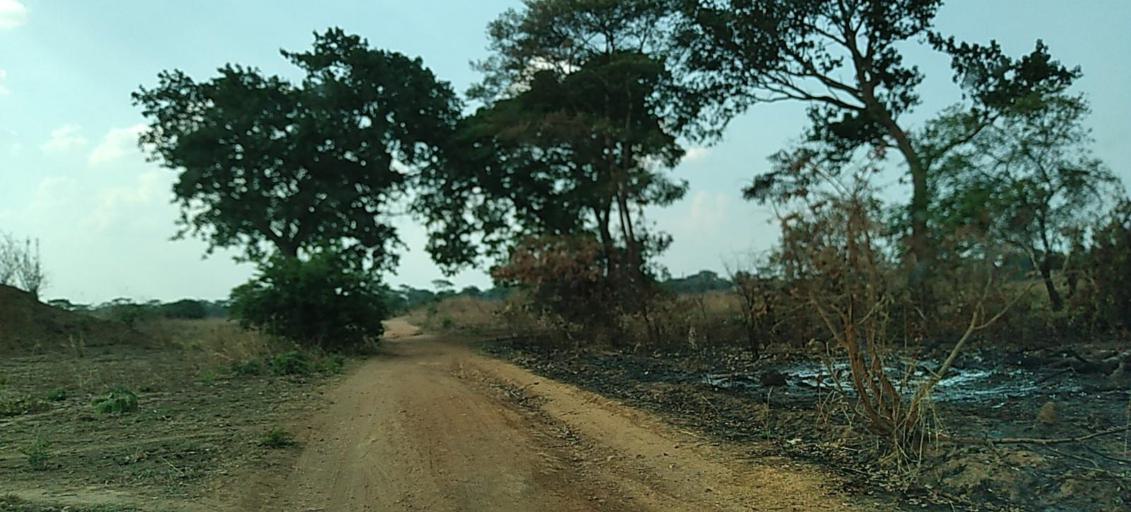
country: ZM
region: Copperbelt
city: Mpongwe
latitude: -13.5020
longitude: 28.0888
